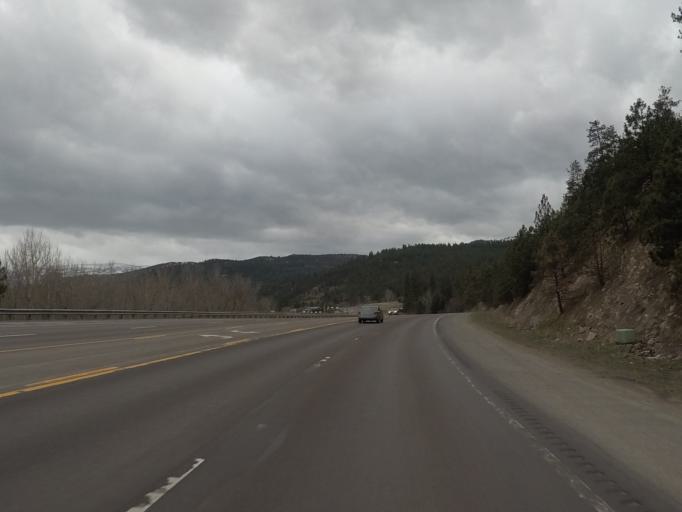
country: US
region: Montana
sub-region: Missoula County
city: Orchard Homes
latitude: 46.8189
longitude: -114.0836
